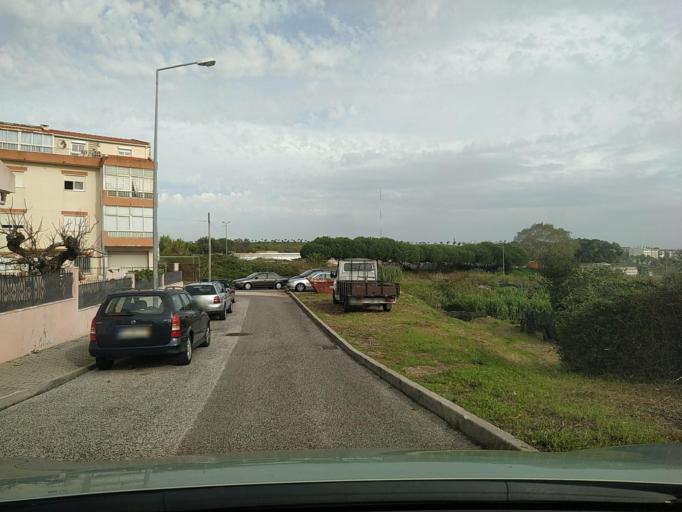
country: PT
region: Lisbon
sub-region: Amadora
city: Amadora
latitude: 38.7733
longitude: -9.2357
